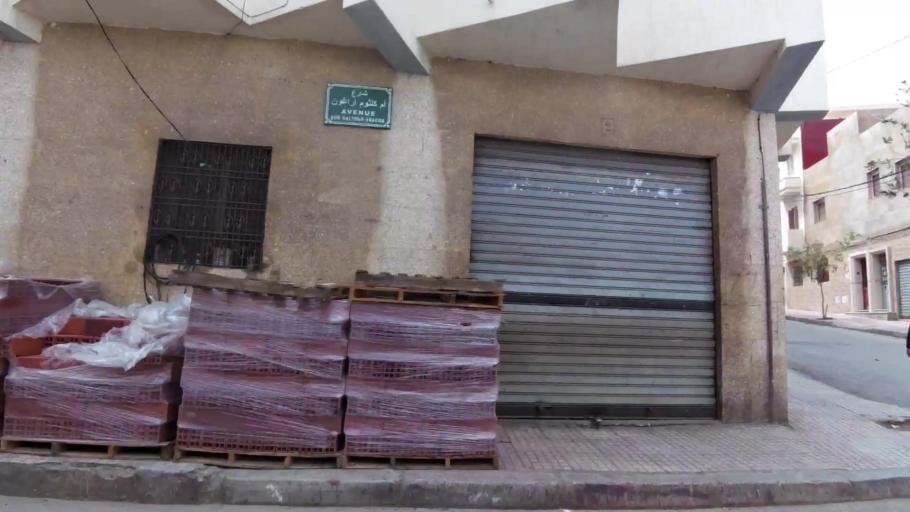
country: MA
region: Tanger-Tetouan
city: Tetouan
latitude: 35.5758
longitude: -5.3606
